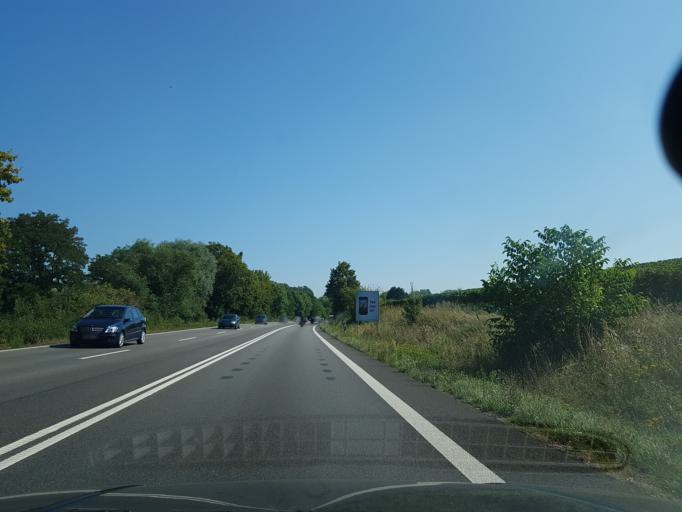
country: DE
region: Rheinland-Pfalz
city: Siebeldingen
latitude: 49.2056
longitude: 8.0609
